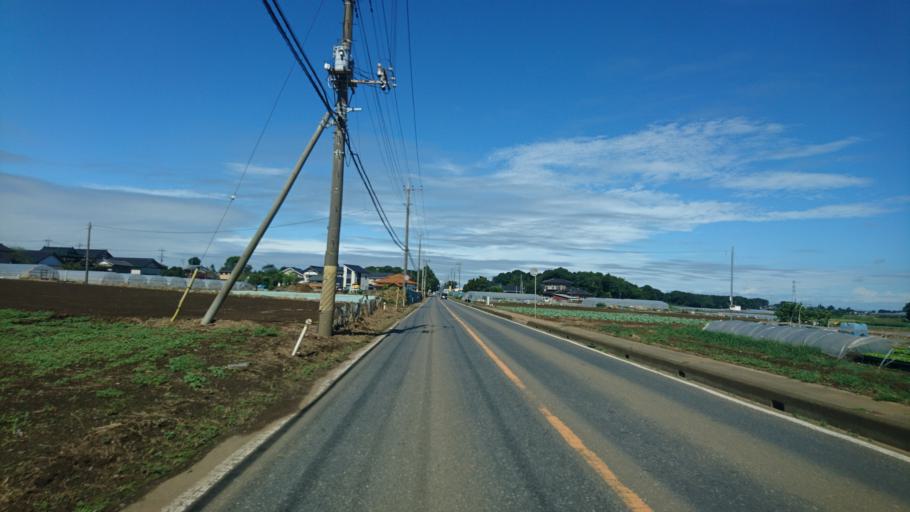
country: JP
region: Ibaraki
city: Ishige
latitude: 36.1431
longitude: 139.9068
